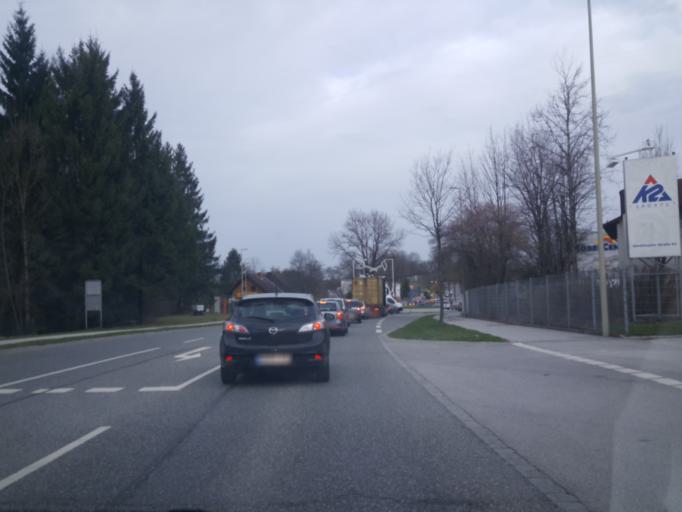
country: DE
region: Bavaria
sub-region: Upper Bavaria
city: Penzberg
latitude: 47.7660
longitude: 11.3559
